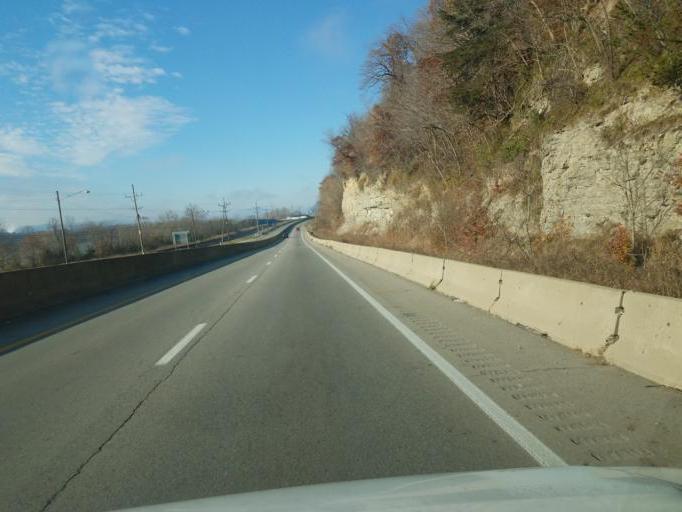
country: US
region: Ohio
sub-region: Scioto County
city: Sciotodale
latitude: 38.7574
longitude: -82.8990
